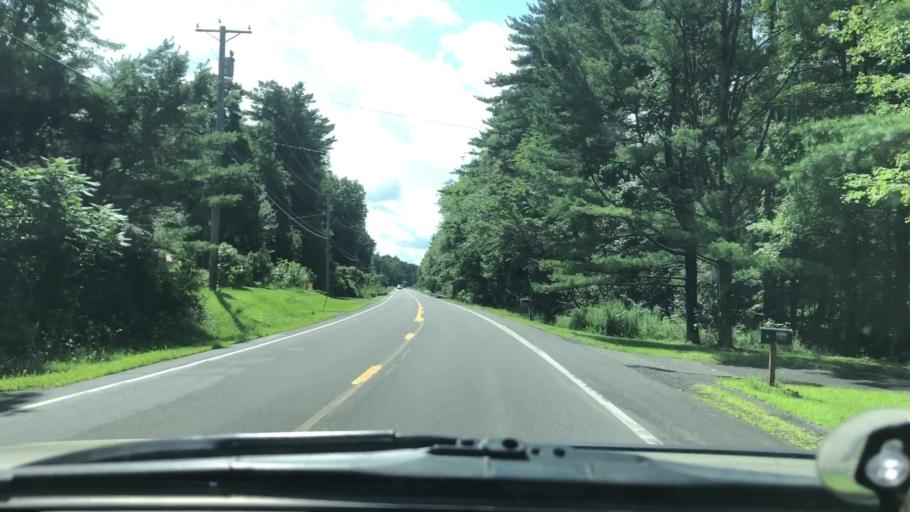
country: US
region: New York
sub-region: Greene County
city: Cairo
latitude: 42.2847
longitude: -73.9838
